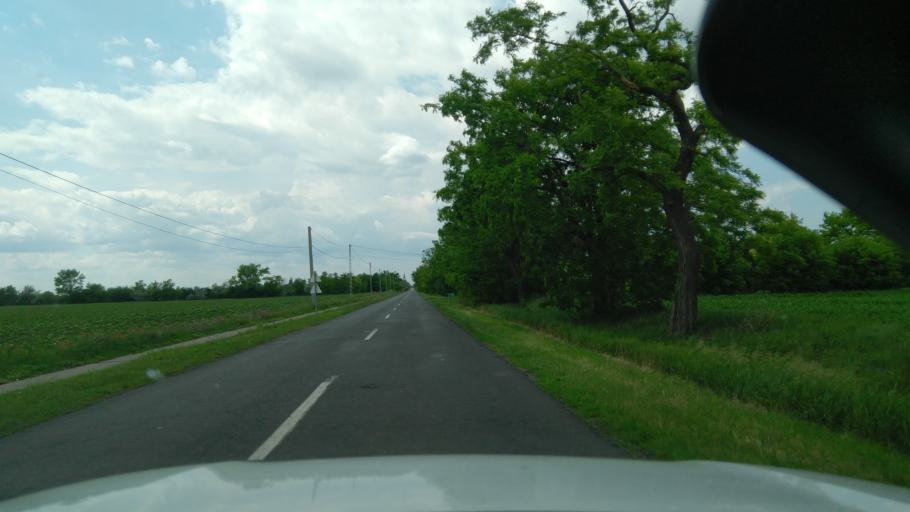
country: HU
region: Bekes
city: Magyarbanhegyes
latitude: 46.4456
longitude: 20.9816
